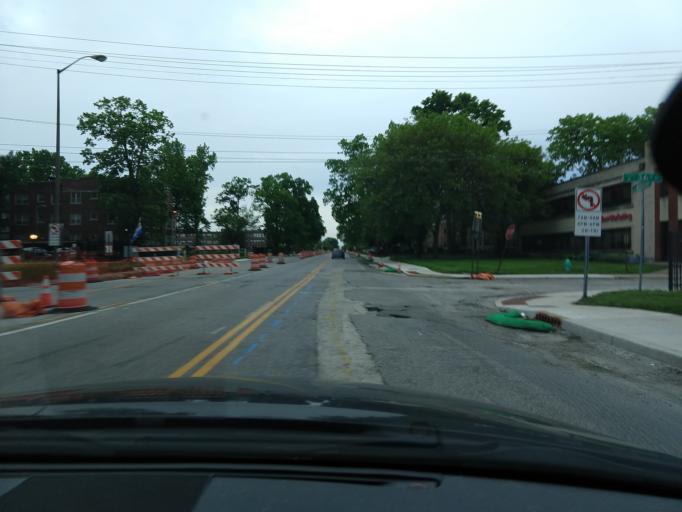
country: US
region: Indiana
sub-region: Marion County
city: Broad Ripple
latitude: 39.8214
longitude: -86.1569
